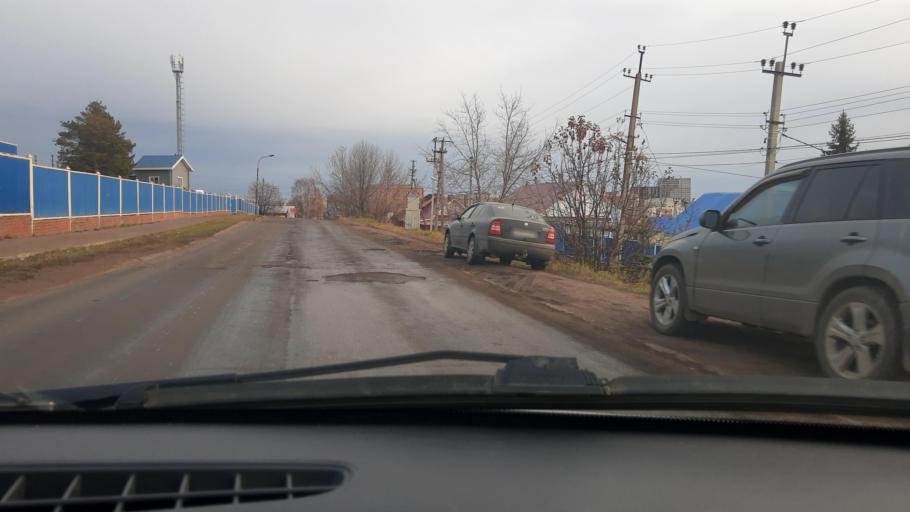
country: RU
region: Bashkortostan
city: Avdon
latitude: 54.6915
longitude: 55.8086
